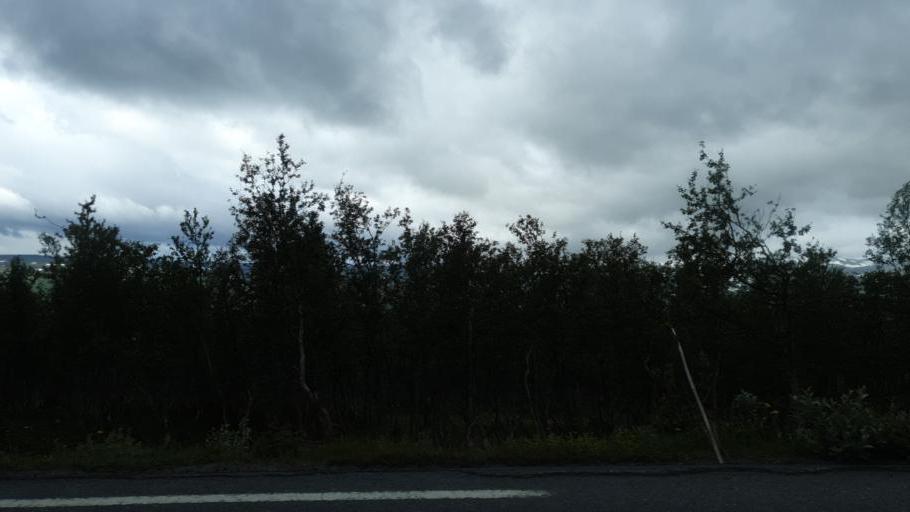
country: NO
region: Oppland
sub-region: Vestre Slidre
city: Slidre
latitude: 61.2679
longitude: 8.8640
